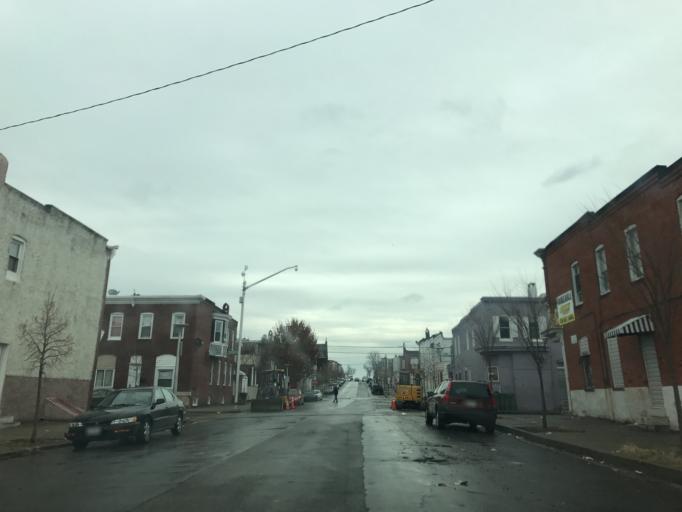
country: US
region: Maryland
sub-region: City of Baltimore
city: Baltimore
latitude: 39.2979
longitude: -76.5791
